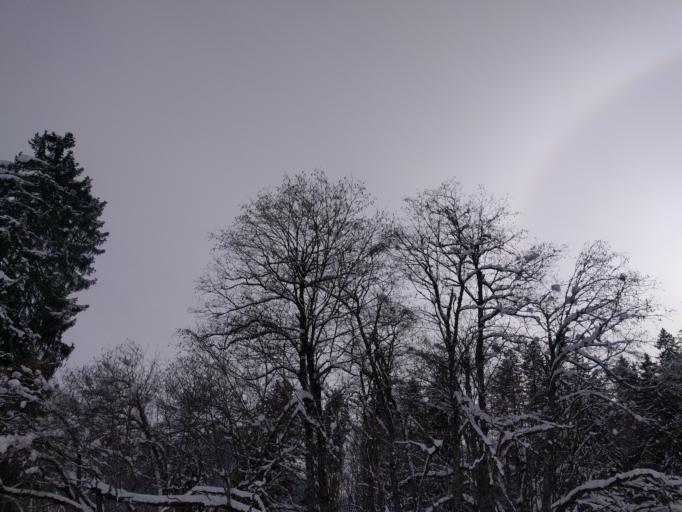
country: AT
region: Styria
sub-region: Politischer Bezirk Liezen
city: Hall
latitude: 47.6918
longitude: 14.4312
